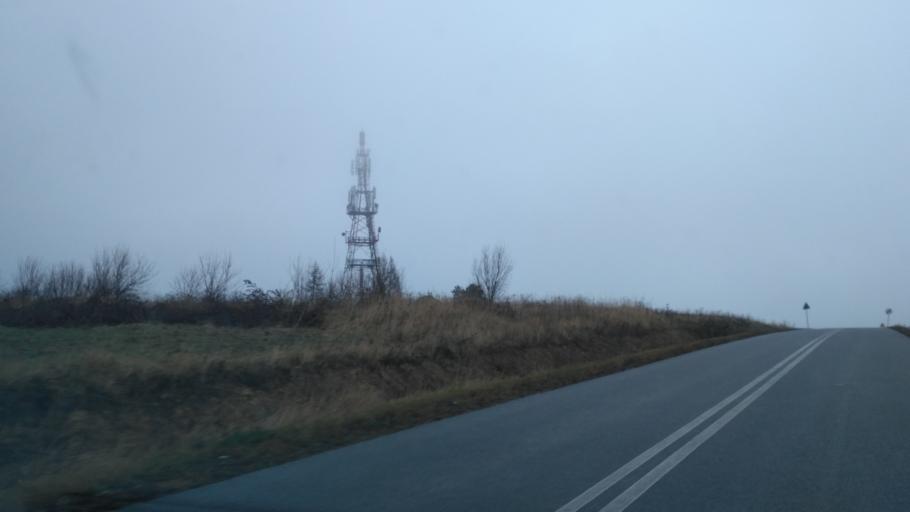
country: PL
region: Subcarpathian Voivodeship
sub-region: Powiat jaroslawski
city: Jodlowka
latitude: 49.8997
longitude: 22.4851
